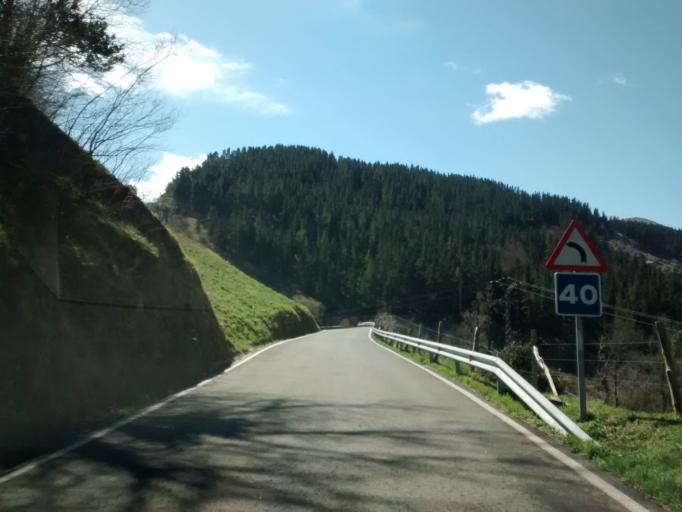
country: ES
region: Cantabria
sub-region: Provincia de Cantabria
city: Lierganes
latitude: 43.2581
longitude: -3.7132
